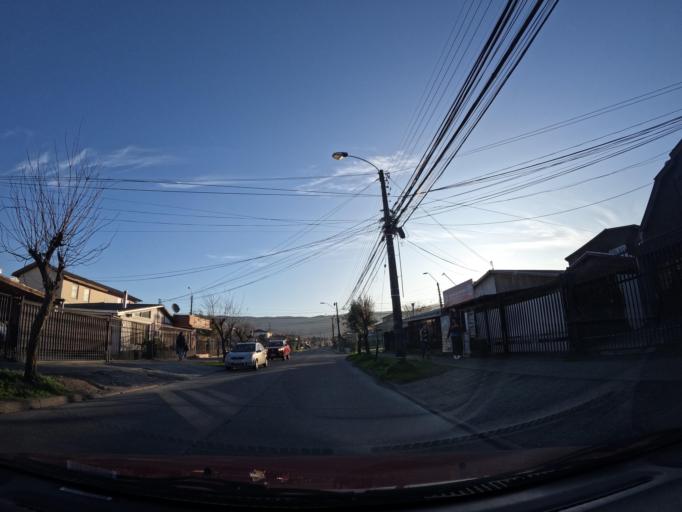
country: CL
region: Biobio
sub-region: Provincia de Concepcion
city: Chiguayante
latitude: -36.9209
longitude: -73.0315
